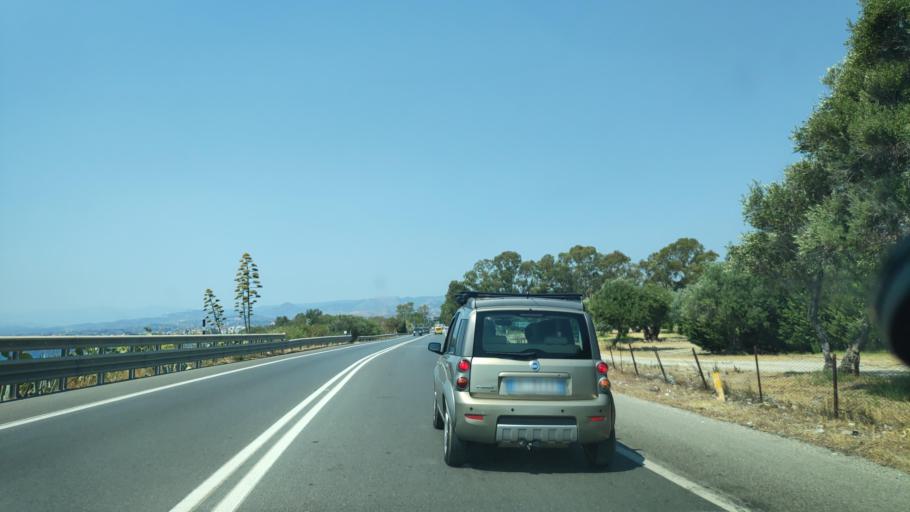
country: IT
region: Calabria
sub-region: Provincia di Reggio Calabria
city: Marina di Gioiosa Ionica
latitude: 38.3061
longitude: 16.3555
